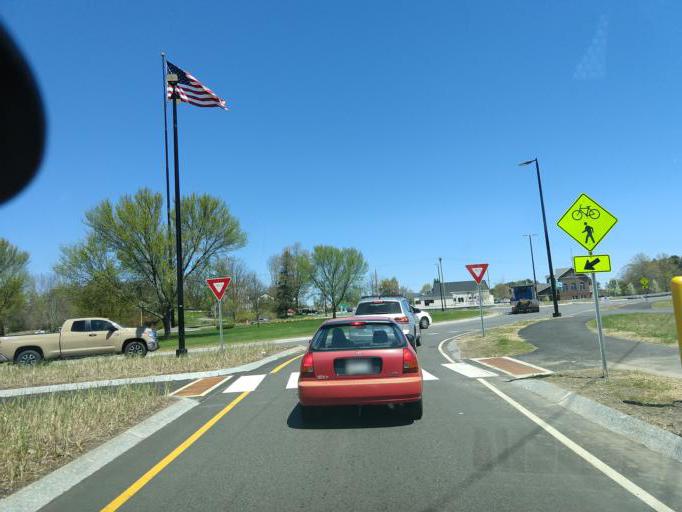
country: US
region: Maine
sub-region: York County
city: Kittery
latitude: 43.1001
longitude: -70.7442
